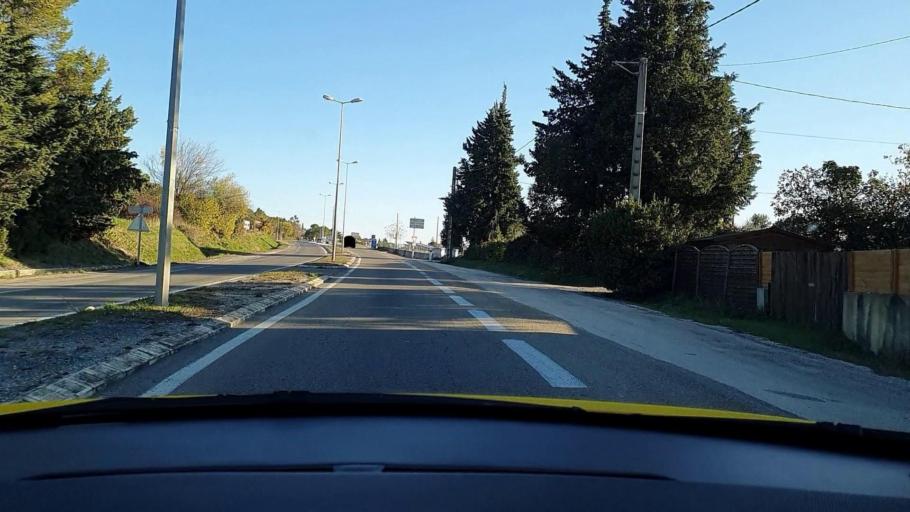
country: FR
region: Languedoc-Roussillon
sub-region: Departement du Gard
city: Saint-Julien-les-Rosiers
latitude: 44.1549
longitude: 4.1100
